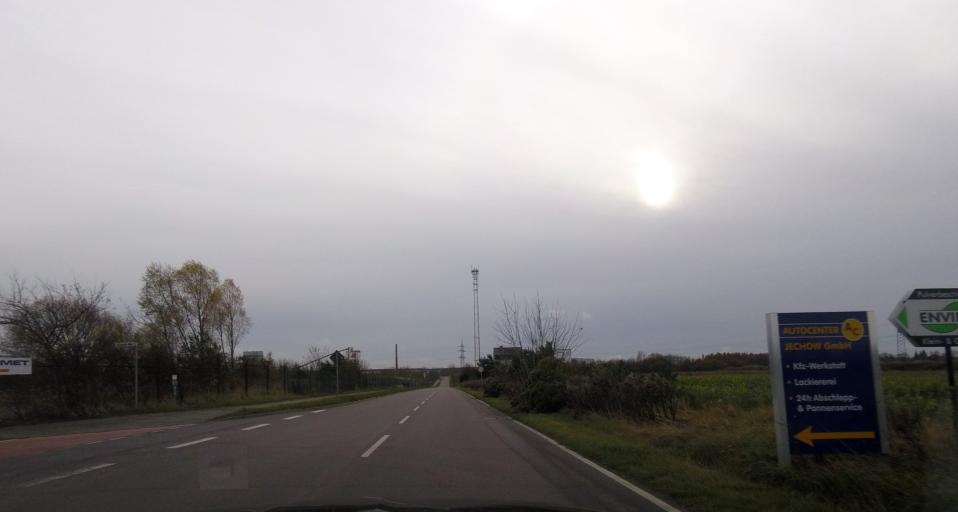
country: DE
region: Brandenburg
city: Niemegk
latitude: 52.0883
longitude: 12.7038
